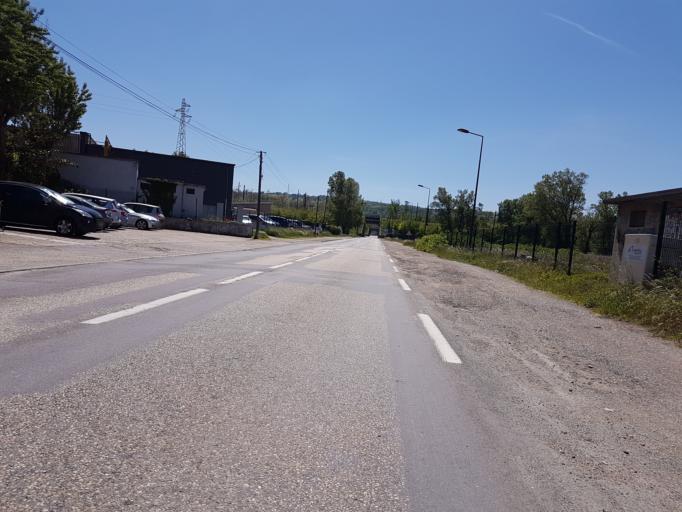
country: FR
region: Rhone-Alpes
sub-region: Departement de l'Isere
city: Chasse-sur-Rhone
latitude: 45.5928
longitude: 4.7896
